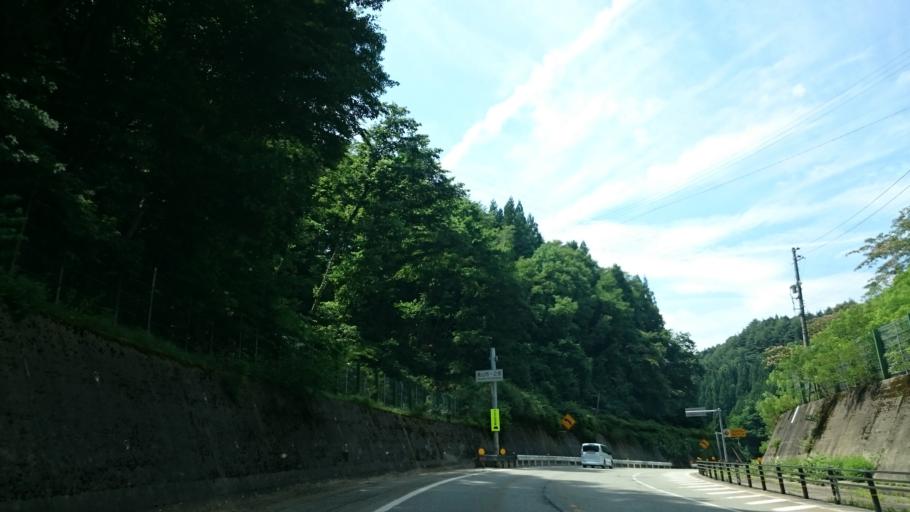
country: JP
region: Gifu
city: Takayama
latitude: 36.0801
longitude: 137.2645
